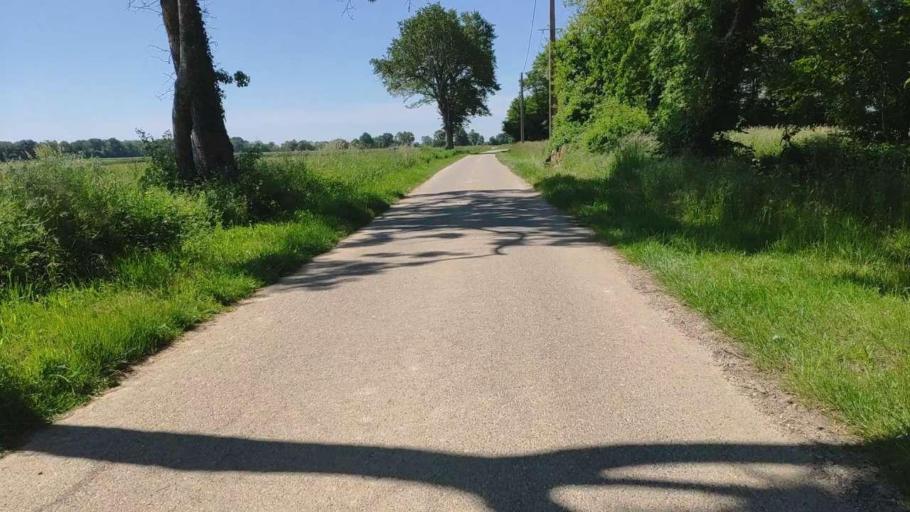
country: FR
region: Franche-Comte
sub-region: Departement du Jura
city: Bletterans
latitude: 46.7744
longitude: 5.4132
